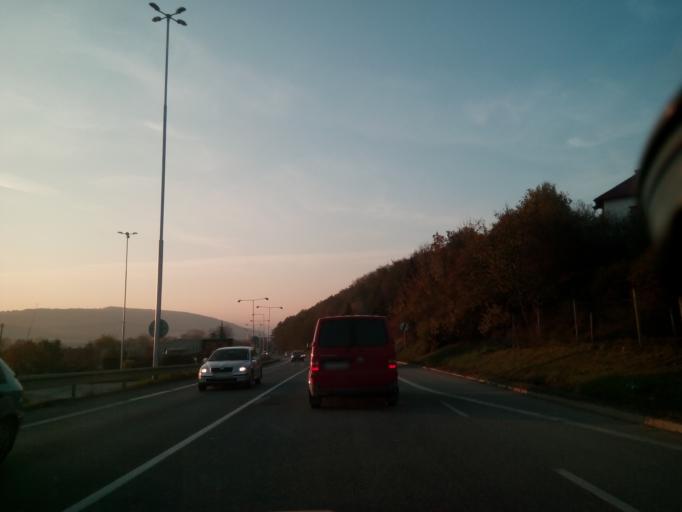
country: SK
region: Presovsky
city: Sabinov
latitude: 49.0040
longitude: 21.0768
